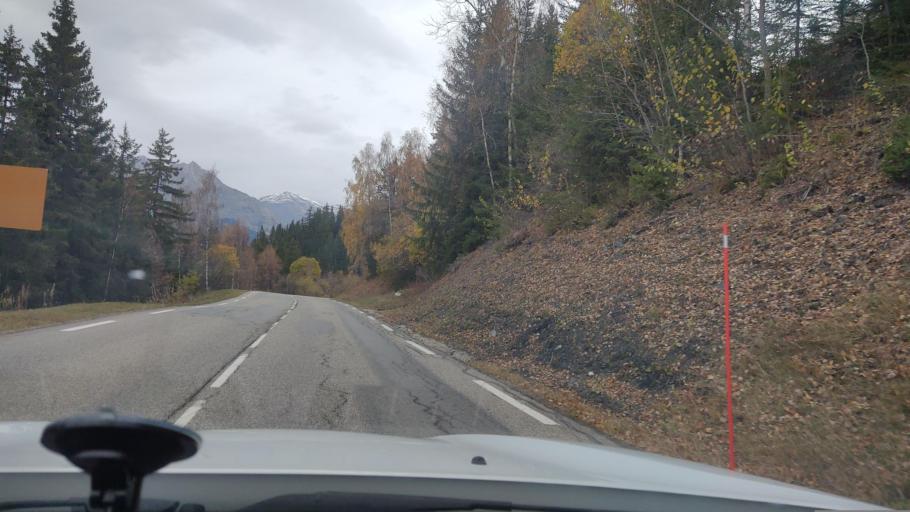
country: FR
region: Rhone-Alpes
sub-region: Departement de la Savoie
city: Bourg-Saint-Maurice
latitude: 45.5814
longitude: 6.7885
